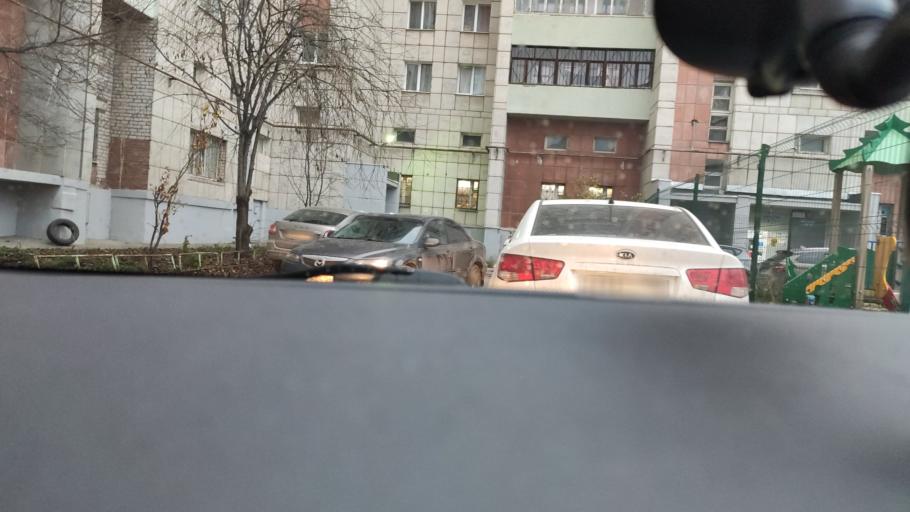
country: RU
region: Perm
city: Perm
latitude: 57.9636
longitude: 56.2006
